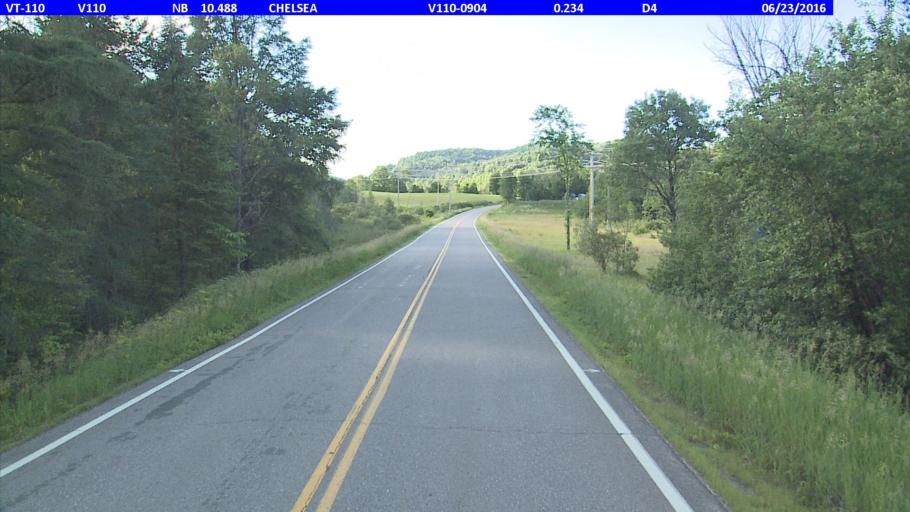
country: US
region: Vermont
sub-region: Orange County
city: Chelsea
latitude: 43.9543
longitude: -72.4641
